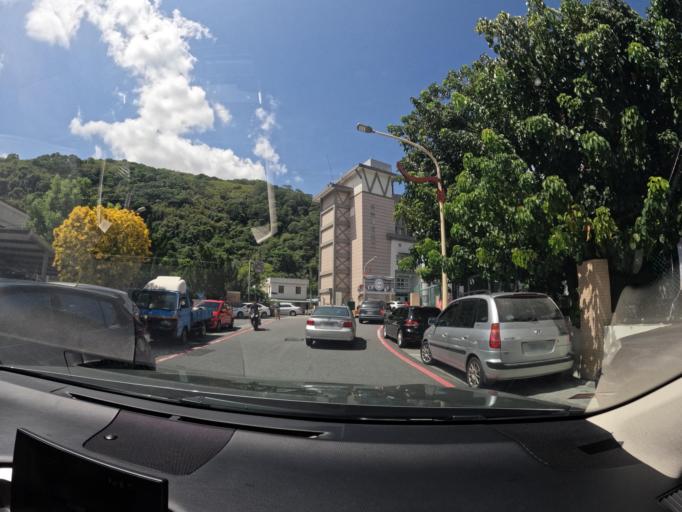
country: TW
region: Taiwan
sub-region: Hualien
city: Hualian
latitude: 23.7149
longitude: 121.4101
